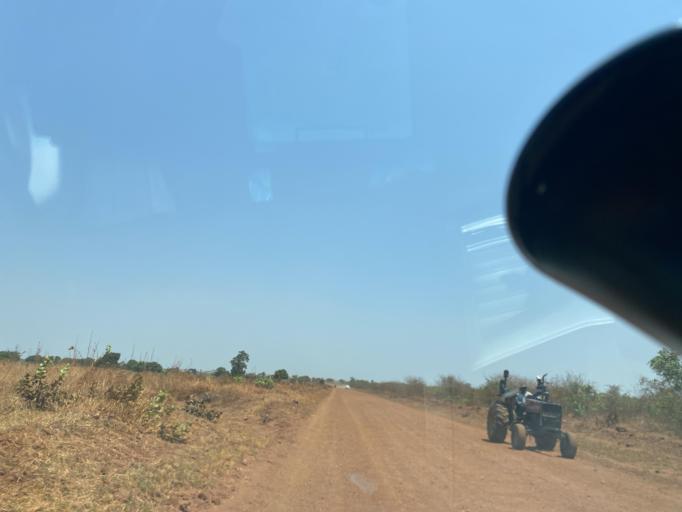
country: ZM
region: Southern
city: Nakambala
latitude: -15.5017
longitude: 27.9143
